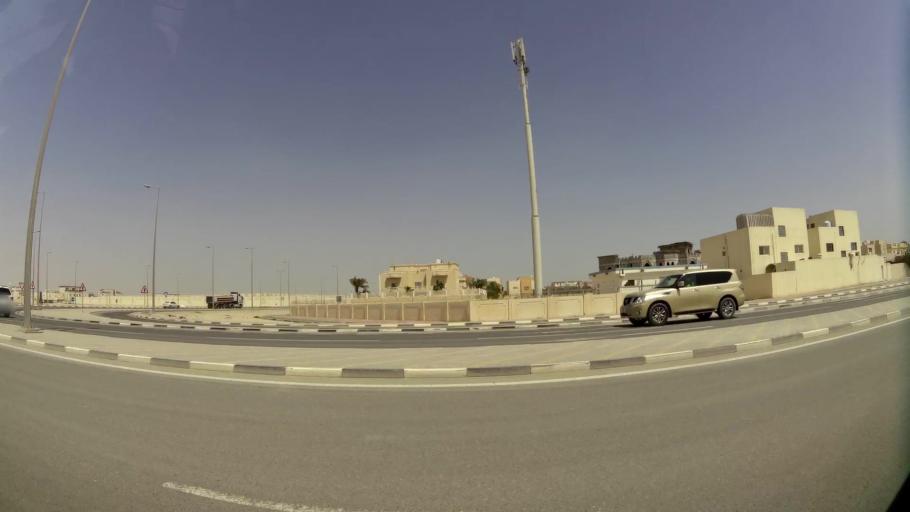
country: QA
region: Baladiyat Umm Salal
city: Umm Salal Muhammad
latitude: 25.3847
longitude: 51.4548
